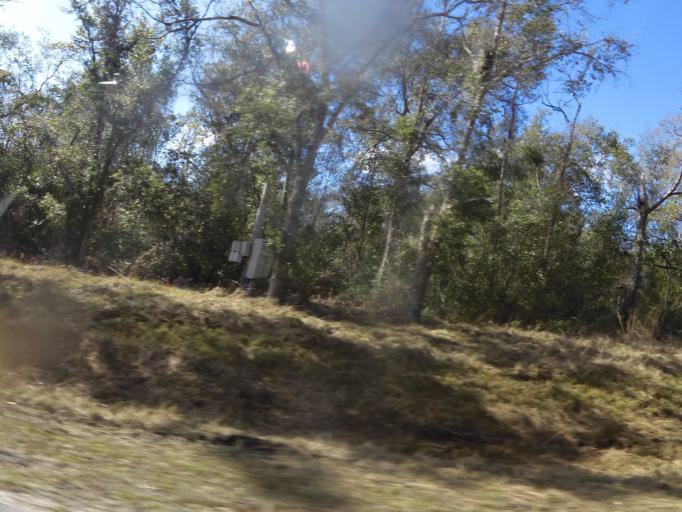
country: US
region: Florida
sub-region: Volusia County
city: Pierson
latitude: 29.2597
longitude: -81.4705
